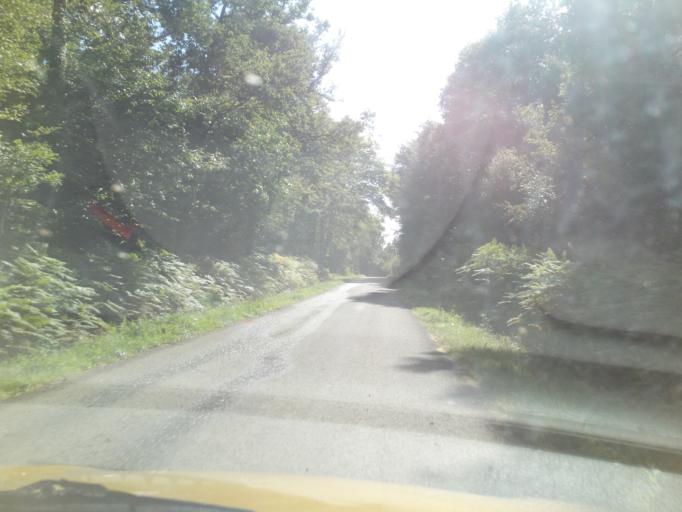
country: FR
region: Brittany
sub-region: Departement du Morbihan
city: Meneac
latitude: 48.1241
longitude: -2.3886
